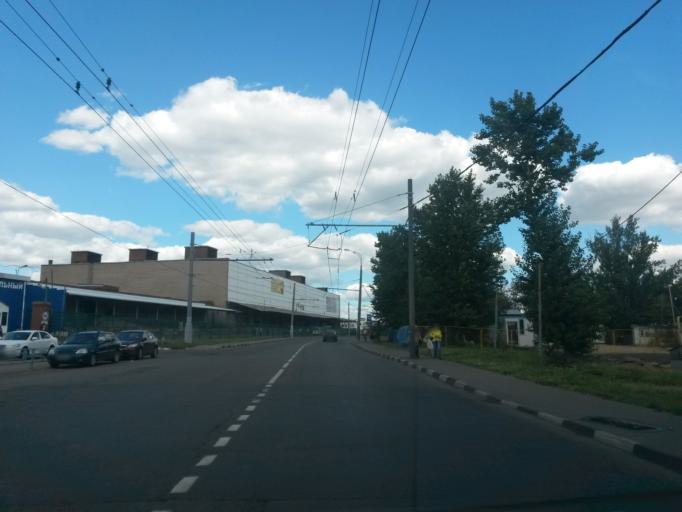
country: RU
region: Moscow
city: Mar'ino
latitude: 55.6547
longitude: 37.7234
